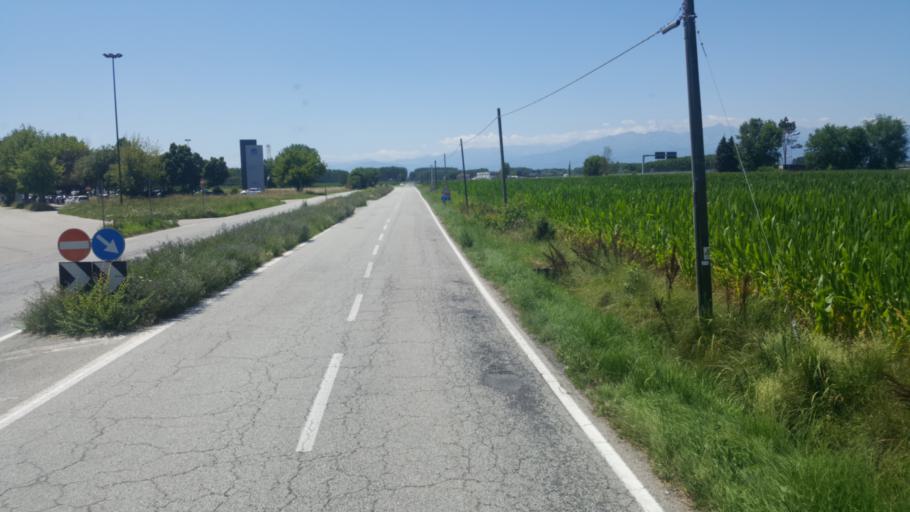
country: IT
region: Piedmont
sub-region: Provincia di Torino
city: Volvera
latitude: 44.9399
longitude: 7.5069
